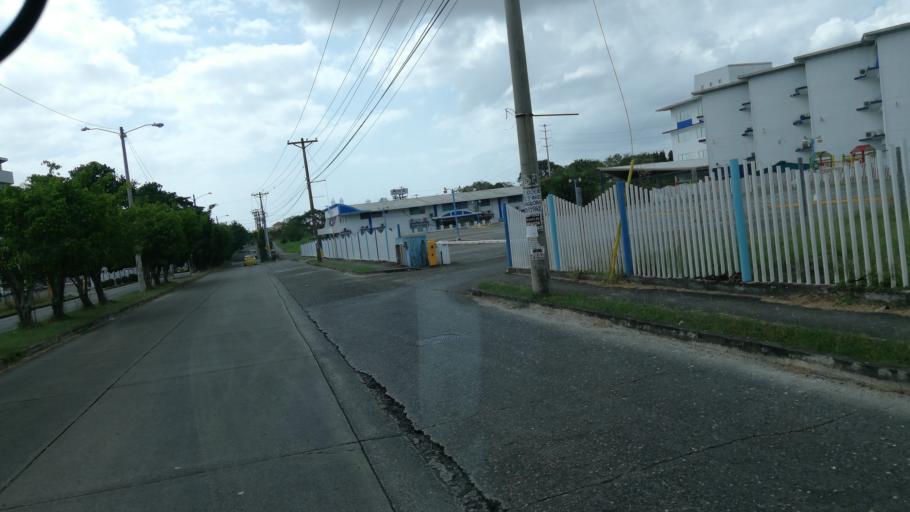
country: PA
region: Panama
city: San Miguelito
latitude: 9.0557
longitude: -79.4598
